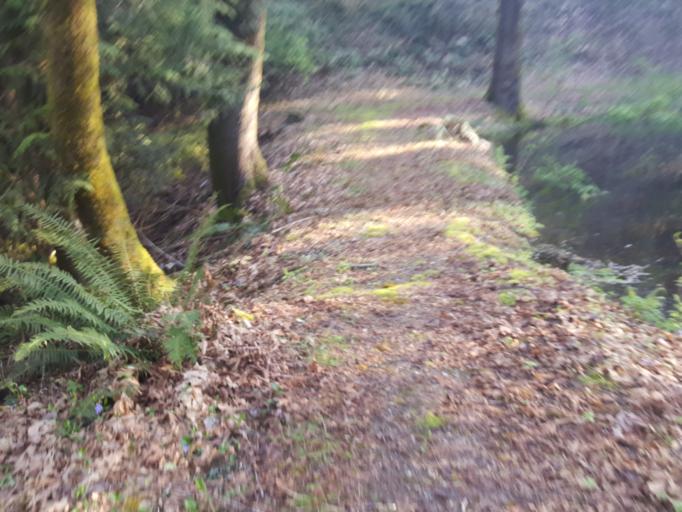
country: US
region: Washington
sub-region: Pierce County
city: Lakewood
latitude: 47.1932
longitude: -122.5239
